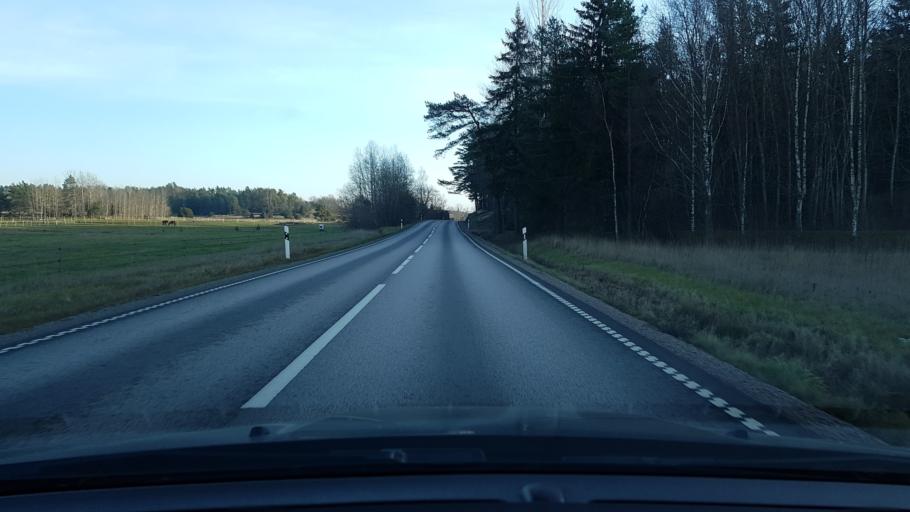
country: SE
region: Stockholm
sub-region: Norrtalje Kommun
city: Nykvarn
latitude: 59.7441
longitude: 18.1232
